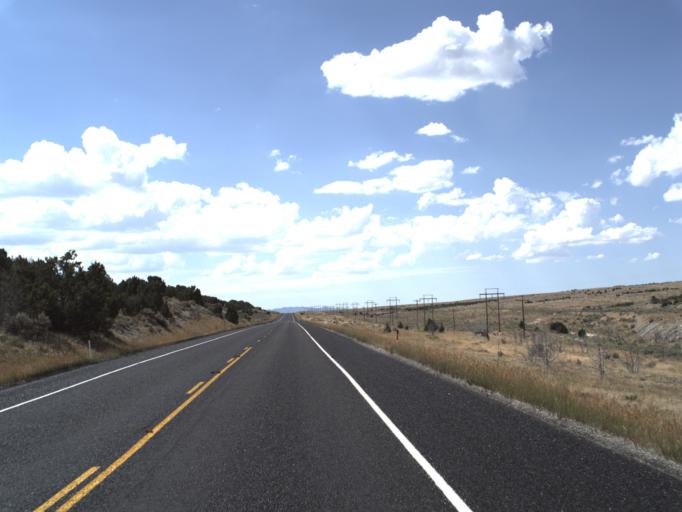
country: US
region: Idaho
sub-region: Minidoka County
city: Rupert
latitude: 41.9761
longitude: -113.1601
